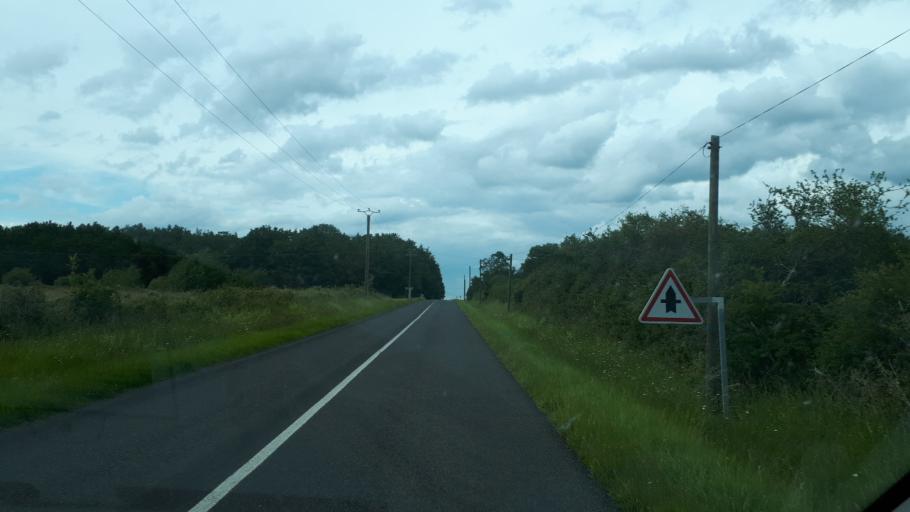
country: FR
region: Centre
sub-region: Departement du Loir-et-Cher
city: Villefranche-sur-Cher
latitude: 47.2391
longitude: 1.7749
